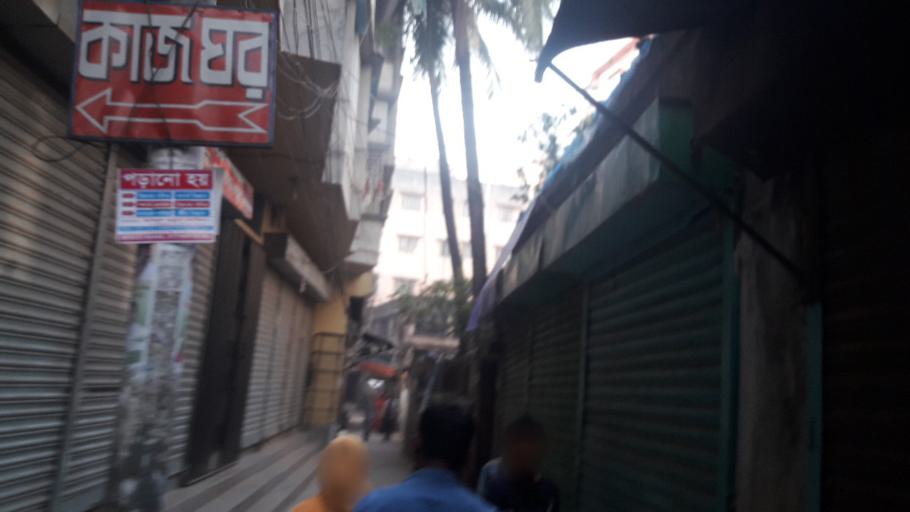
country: BD
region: Dhaka
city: Azimpur
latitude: 23.7232
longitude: 90.3764
